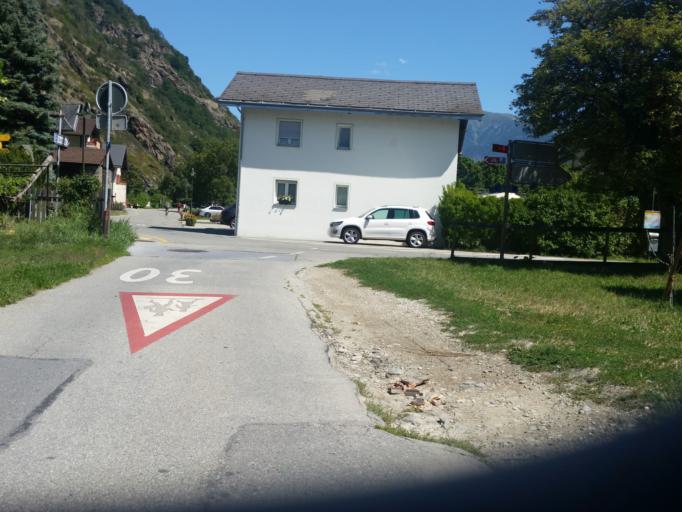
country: CH
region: Valais
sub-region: Visp District
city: Visp
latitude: 46.2995
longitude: 7.9180
